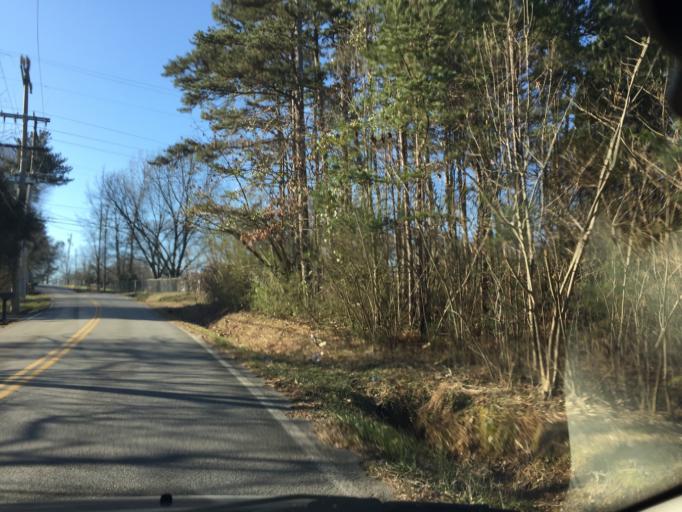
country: US
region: Tennessee
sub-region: Hamilton County
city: Harrison
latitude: 35.0691
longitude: -85.1100
